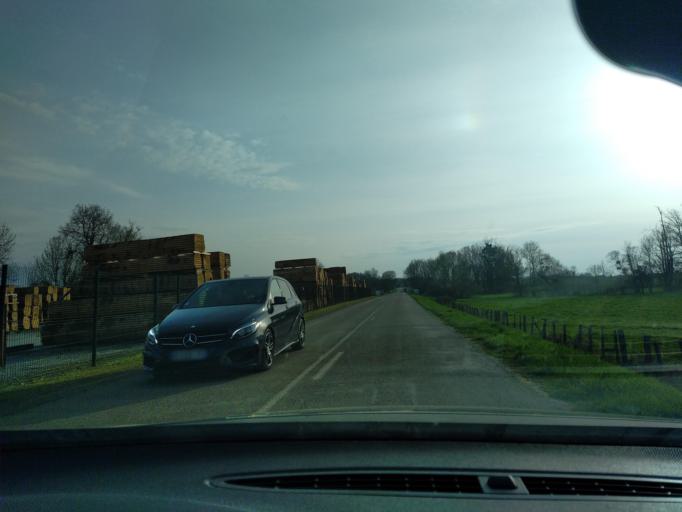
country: FR
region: Franche-Comte
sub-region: Departement du Jura
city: Chaussin
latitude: 46.9876
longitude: 5.4516
